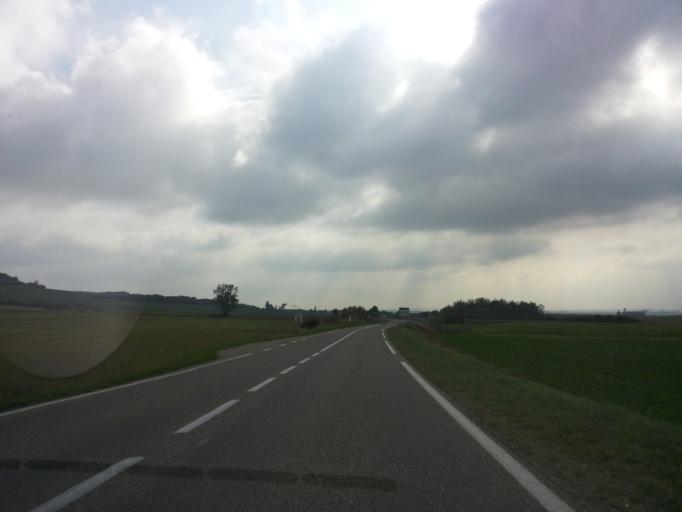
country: FR
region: Lorraine
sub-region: Departement de la Moselle
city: Solgne
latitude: 48.9237
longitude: 6.3322
